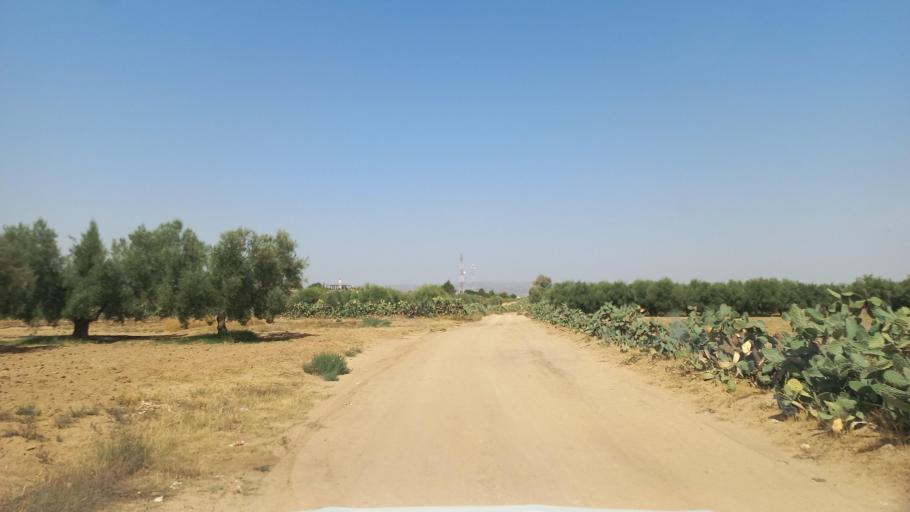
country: TN
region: Al Qasrayn
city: Kasserine
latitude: 35.2497
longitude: 9.0322
